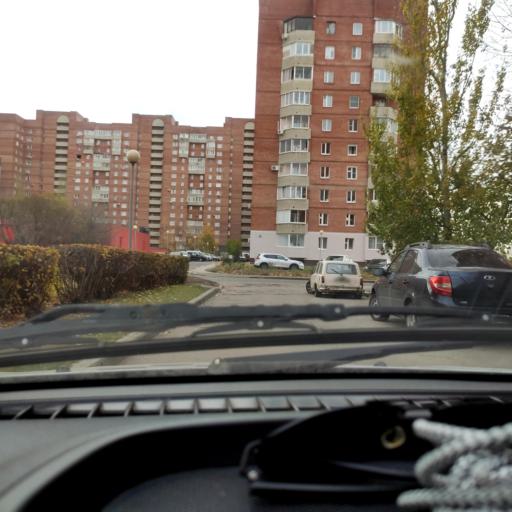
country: RU
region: Samara
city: Tol'yatti
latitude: 53.5026
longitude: 49.2770
